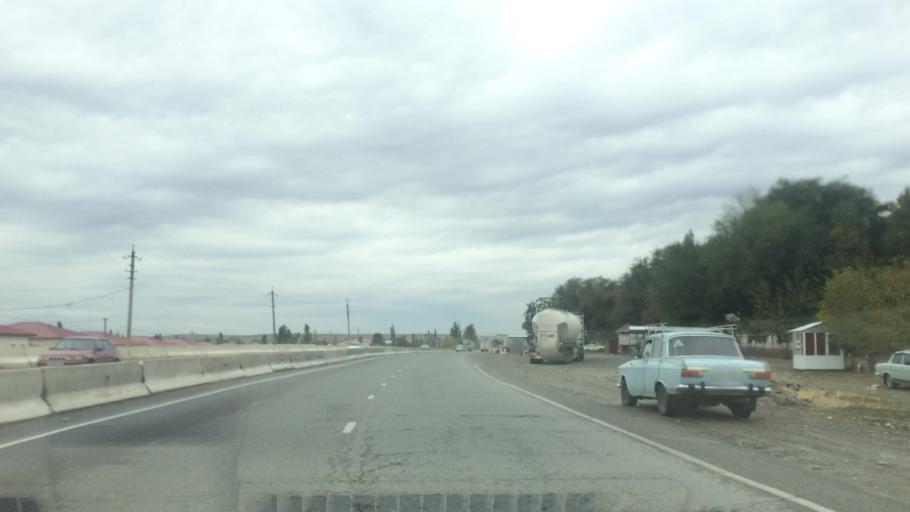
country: UZ
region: Jizzax
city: Jizzax
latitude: 39.9739
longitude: 67.5603
